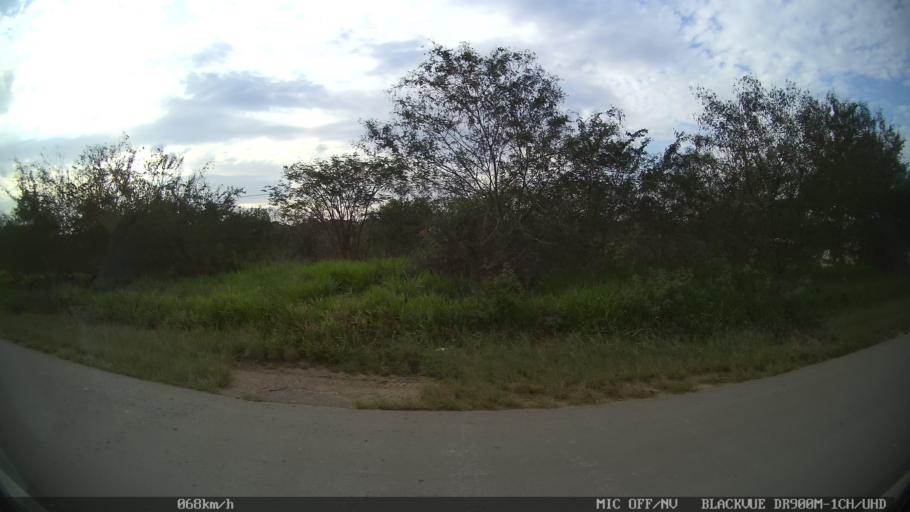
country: BR
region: Sao Paulo
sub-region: Cosmopolis
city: Cosmopolis
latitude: -22.6293
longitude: -47.2818
